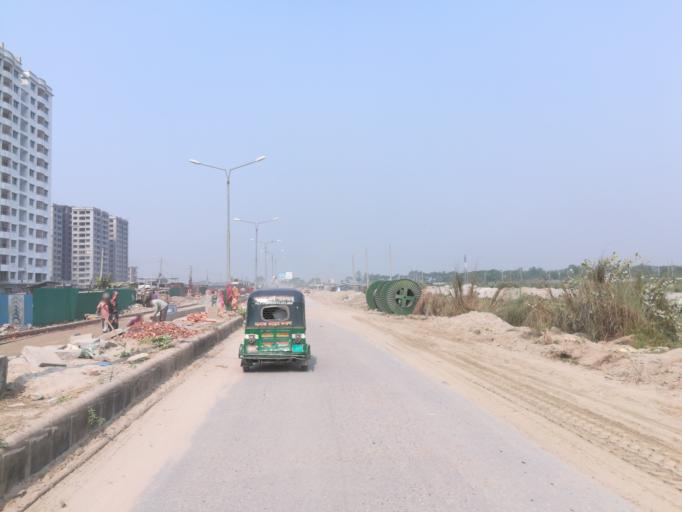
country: BD
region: Dhaka
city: Tungi
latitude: 23.8590
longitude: 90.3539
